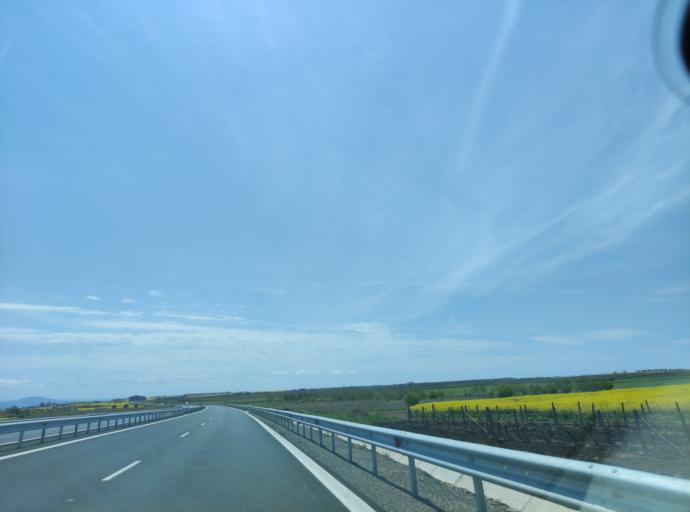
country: BG
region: Burgas
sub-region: Obshtina Pomorie
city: Pomorie
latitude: 42.5766
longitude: 27.5772
